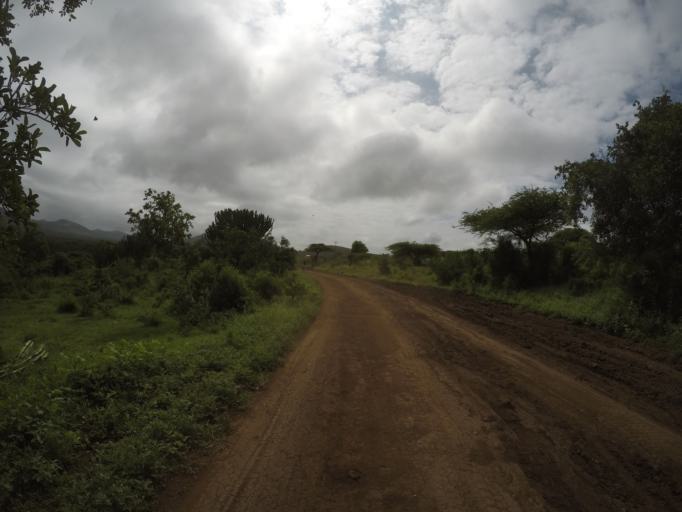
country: ZA
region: KwaZulu-Natal
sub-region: uThungulu District Municipality
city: Empangeni
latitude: -28.6220
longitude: 31.8696
